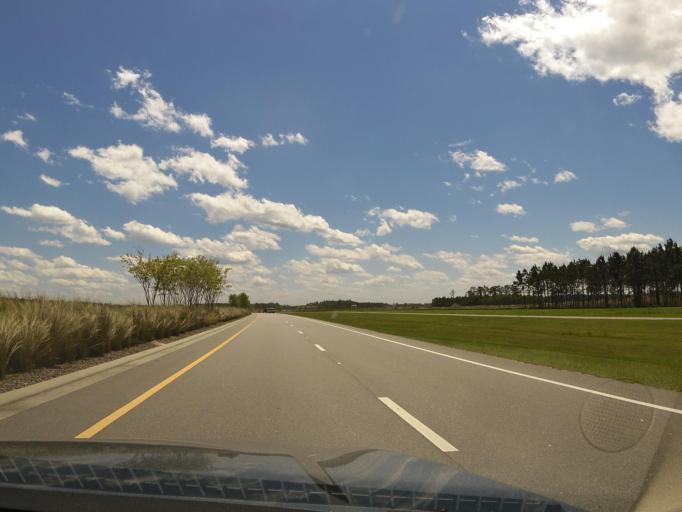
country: US
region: Florida
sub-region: Saint Johns County
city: Fruit Cove
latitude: 30.0077
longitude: -81.5057
